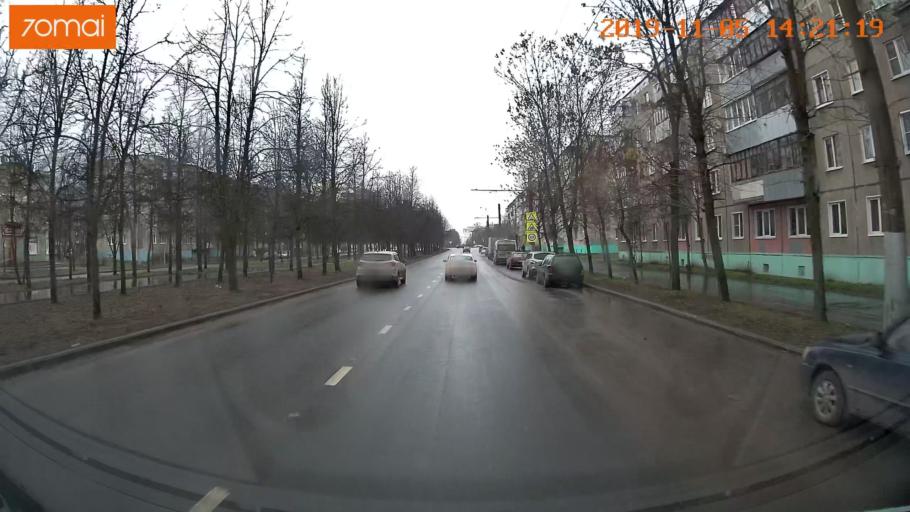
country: RU
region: Ivanovo
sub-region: Gorod Ivanovo
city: Ivanovo
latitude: 56.9586
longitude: 41.0117
